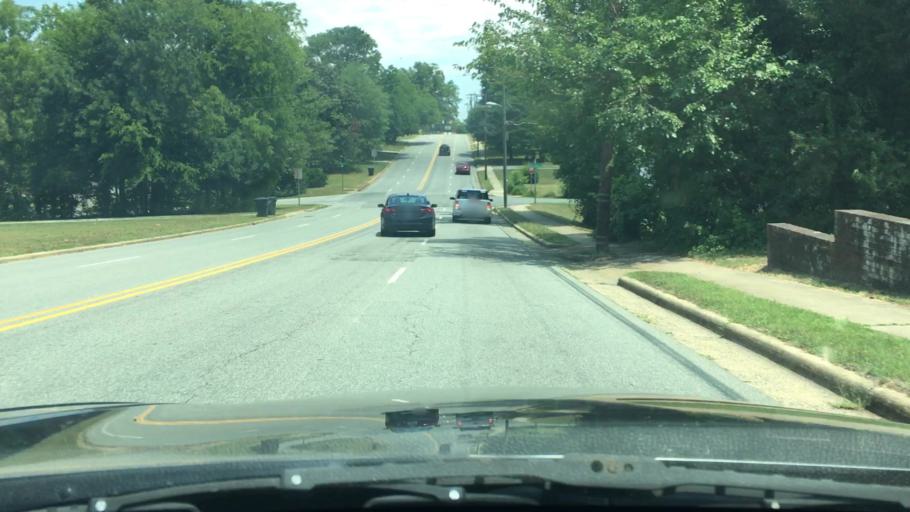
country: US
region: North Carolina
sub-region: Alamance County
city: Graham
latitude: 36.0933
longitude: -79.4099
